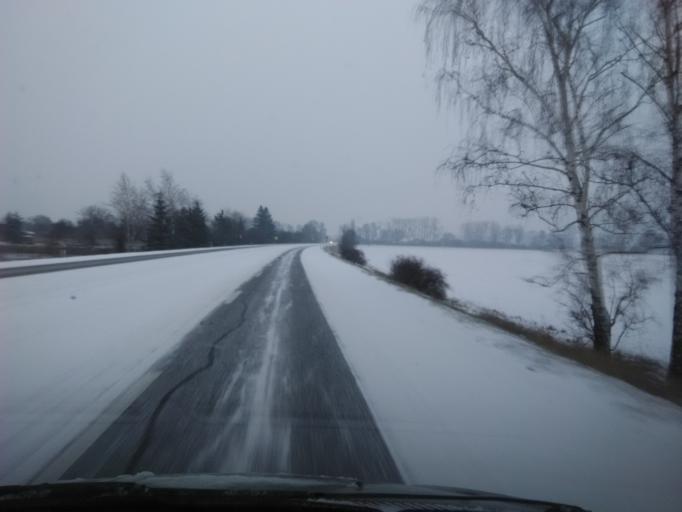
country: CZ
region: Olomoucky
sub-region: Okres Prerov
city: Hranice
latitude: 49.5468
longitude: 17.6834
